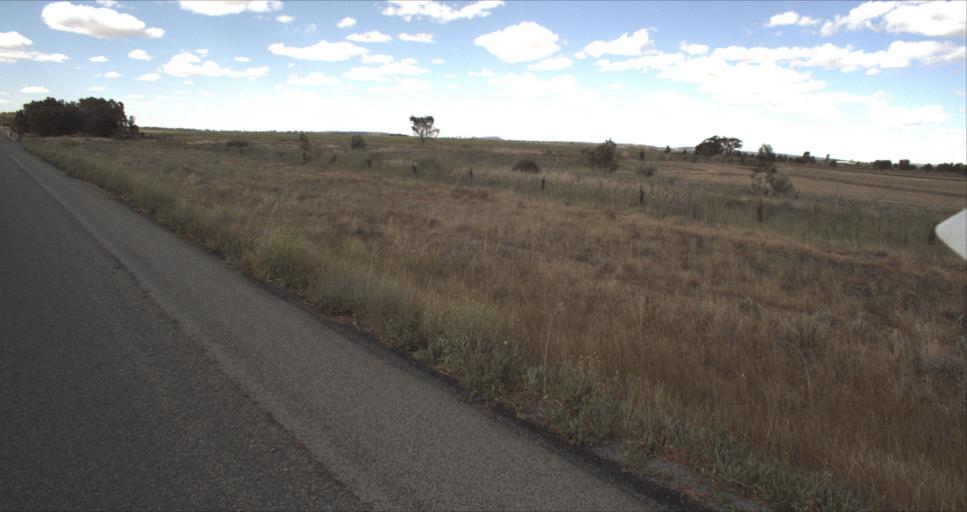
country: AU
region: New South Wales
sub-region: Leeton
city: Leeton
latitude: -34.4421
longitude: 146.2562
